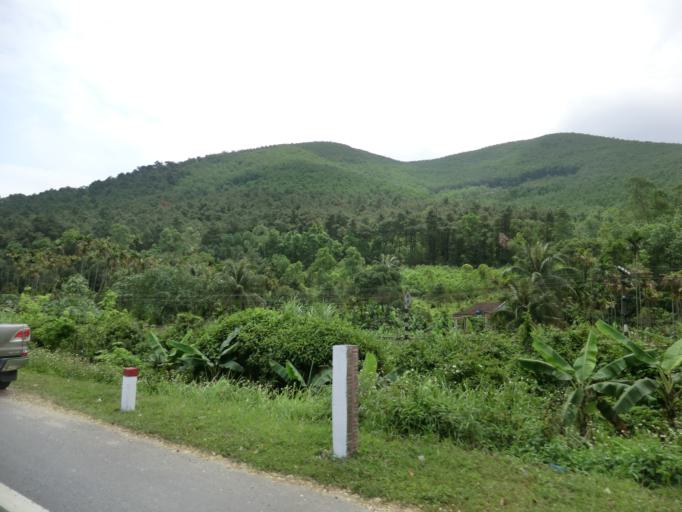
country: VN
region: Thua Thien-Hue
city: Phu Loc
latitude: 16.2859
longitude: 107.8457
